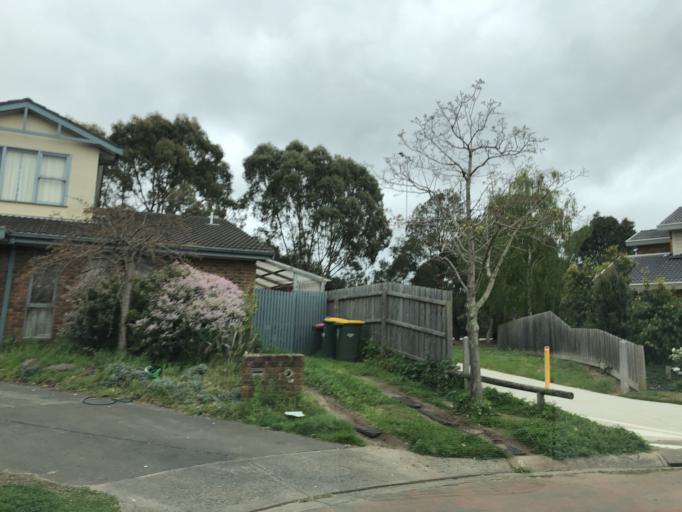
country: AU
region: Victoria
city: Burwood East
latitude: -37.8589
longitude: 145.1606
